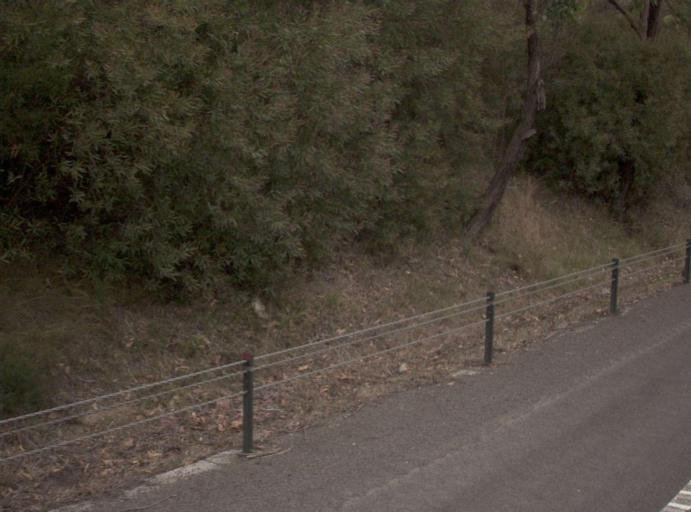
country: AU
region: Victoria
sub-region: Latrobe
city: Moe
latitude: -38.2114
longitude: 146.3224
